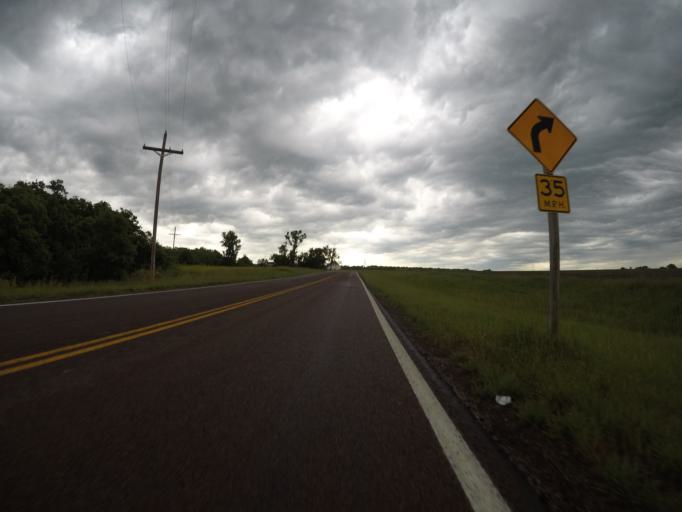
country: US
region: Kansas
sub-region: Shawnee County
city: Rossville
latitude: 38.9592
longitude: -96.0210
